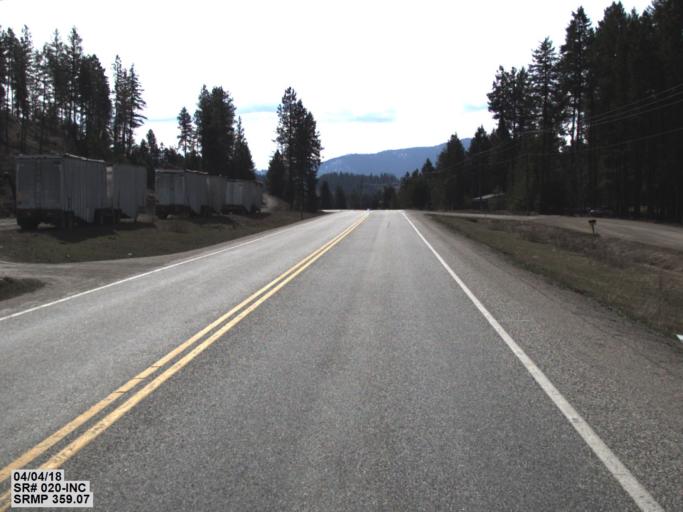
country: US
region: Washington
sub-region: Stevens County
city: Colville
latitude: 48.5277
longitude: -117.8196
